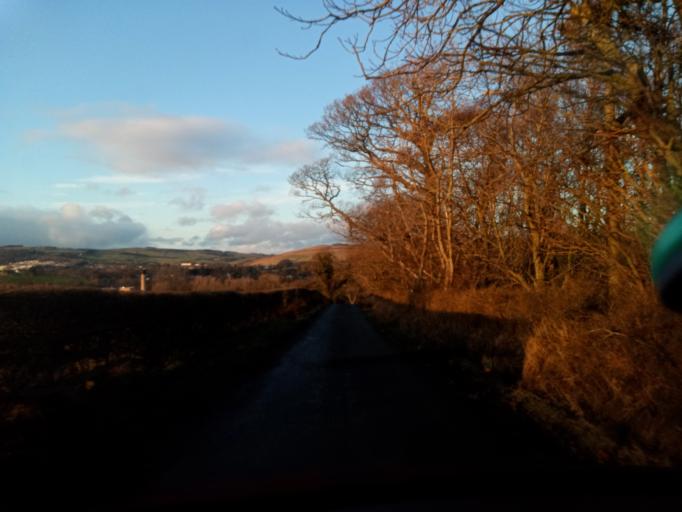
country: GB
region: Scotland
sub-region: The Scottish Borders
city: Melrose
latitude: 55.5922
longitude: -2.7365
